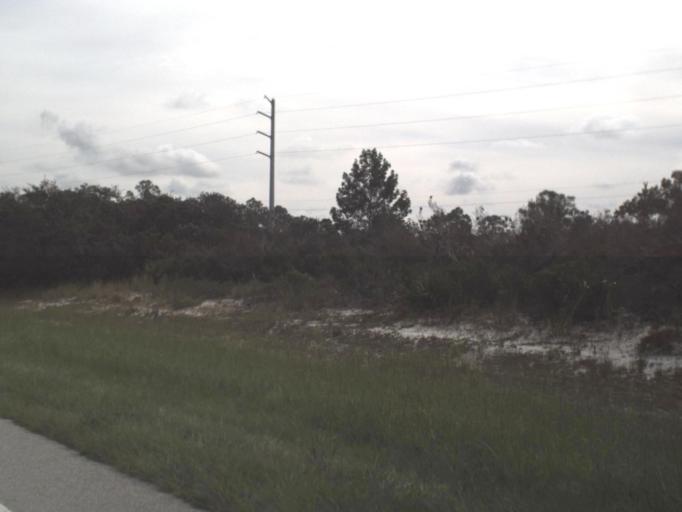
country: US
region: Florida
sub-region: Highlands County
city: Placid Lakes
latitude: 27.2094
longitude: -81.3567
